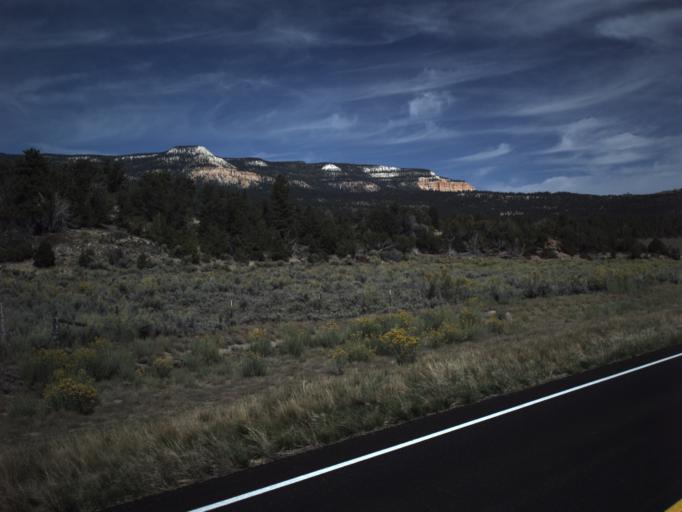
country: US
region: Utah
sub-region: Garfield County
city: Panguitch
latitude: 37.6651
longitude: -111.8318
